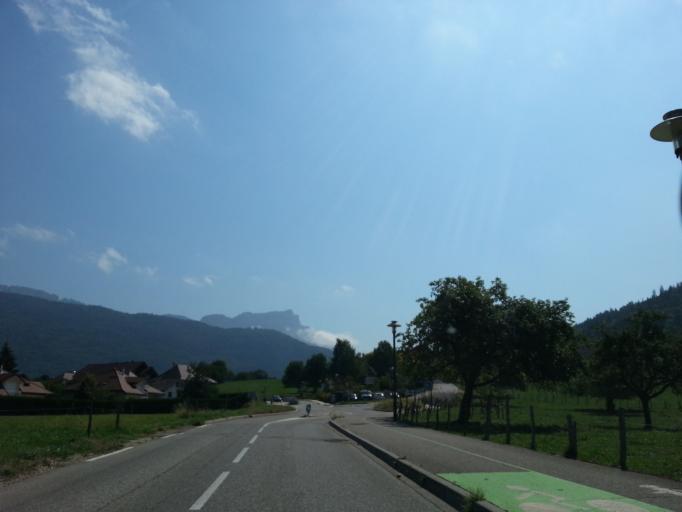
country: FR
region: Rhone-Alpes
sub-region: Departement de la Haute-Savoie
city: Annecy-le-Vieux
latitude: 45.9218
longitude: 6.1688
